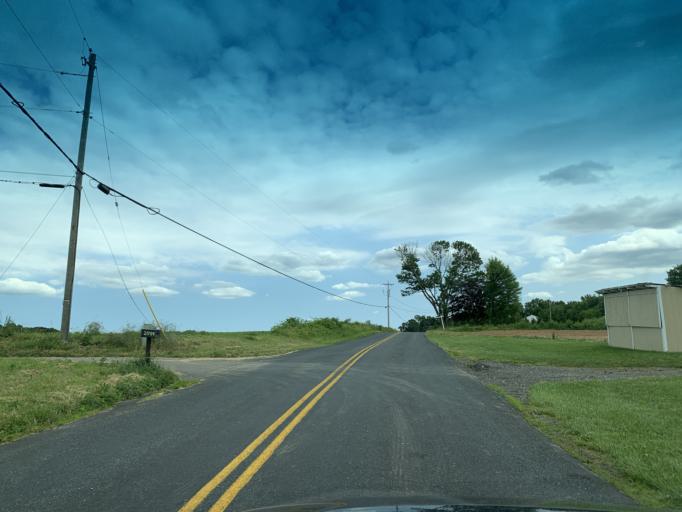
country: US
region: Maryland
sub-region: Harford County
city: Jarrettsville
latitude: 39.6179
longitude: -76.4994
